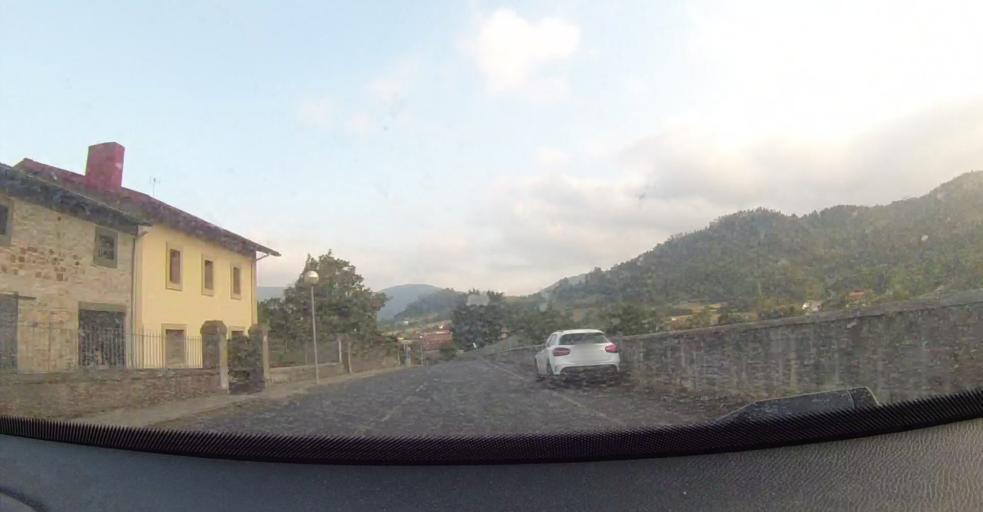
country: ES
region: Basque Country
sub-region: Bizkaia
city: Sopuerta
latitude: 43.2785
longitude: -3.1596
